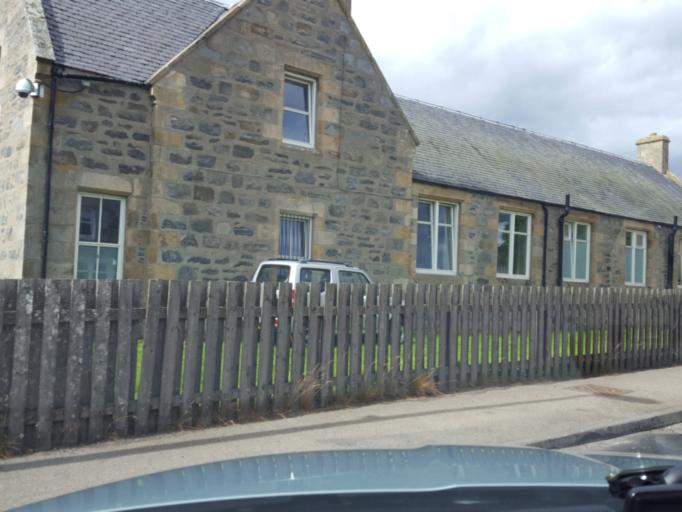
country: GB
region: Scotland
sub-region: Highland
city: Grantown on Spey
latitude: 57.3380
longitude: -3.5379
